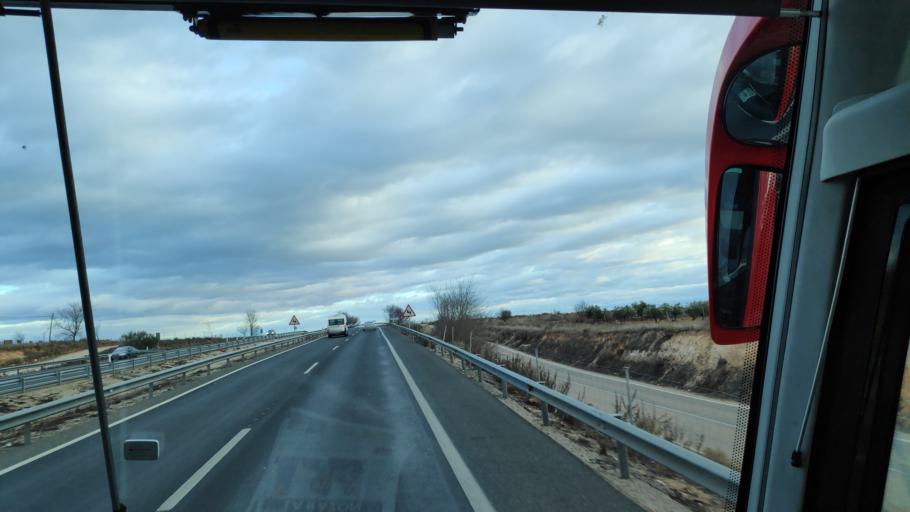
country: ES
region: Madrid
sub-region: Provincia de Madrid
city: Villarejo de Salvanes
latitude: 40.1589
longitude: -3.2612
